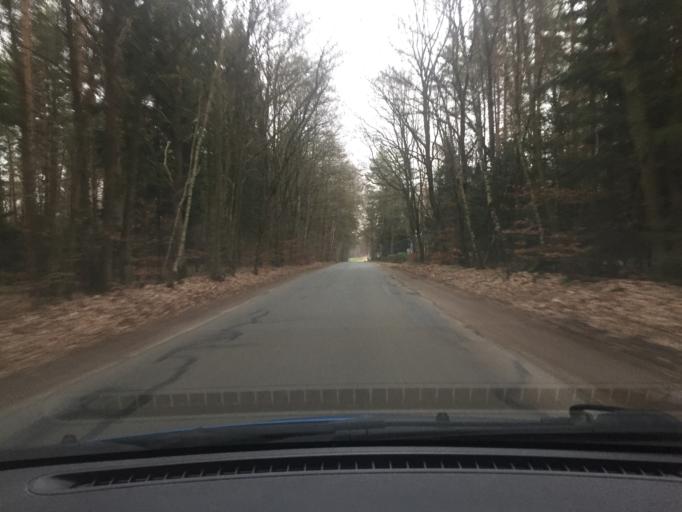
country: DE
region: Lower Saxony
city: Jelmstorf
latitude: 53.1027
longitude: 10.5309
